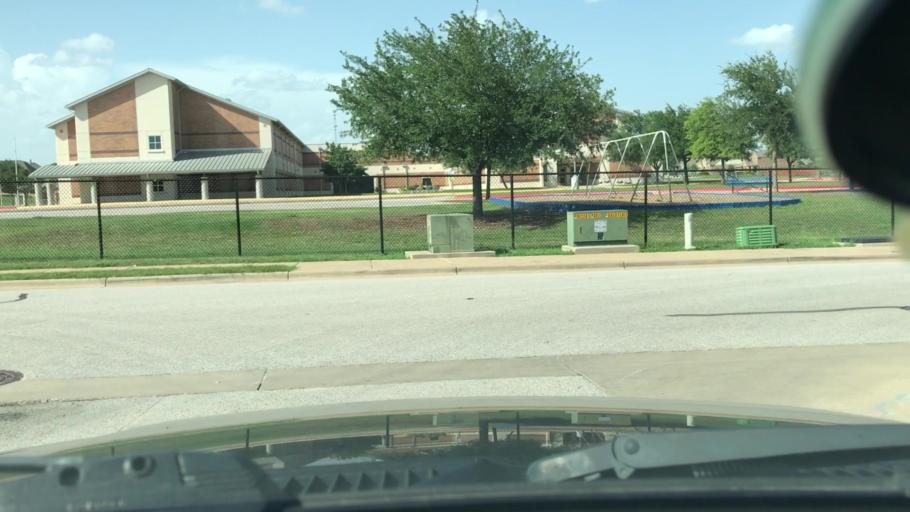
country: US
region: Texas
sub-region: Williamson County
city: Leander
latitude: 30.5368
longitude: -97.8668
